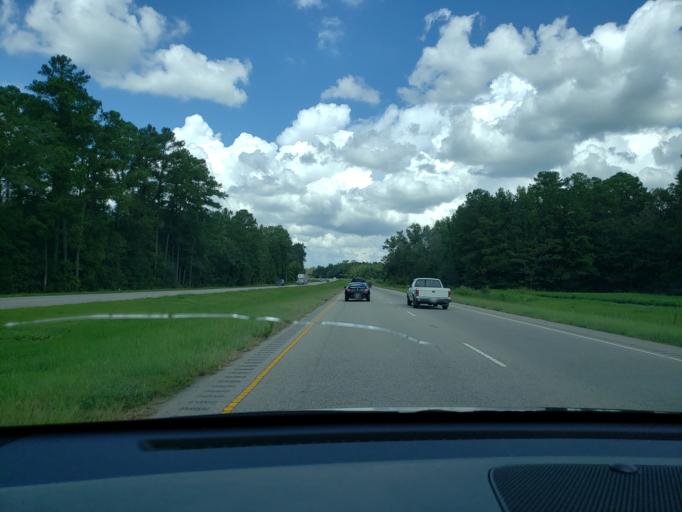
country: US
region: North Carolina
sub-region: Bladen County
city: Elizabethtown
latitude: 34.6974
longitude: -78.7399
